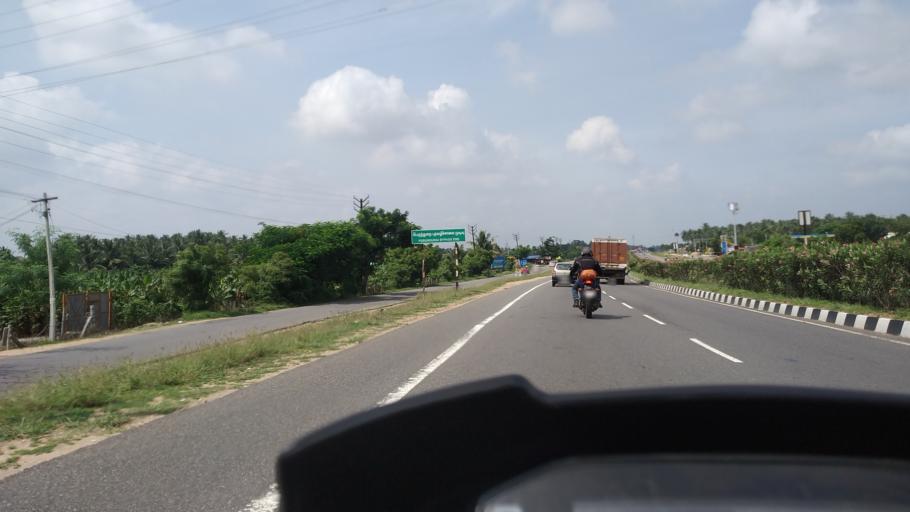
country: IN
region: Tamil Nadu
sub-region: Erode
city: Perundurai
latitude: 11.2563
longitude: 77.5483
